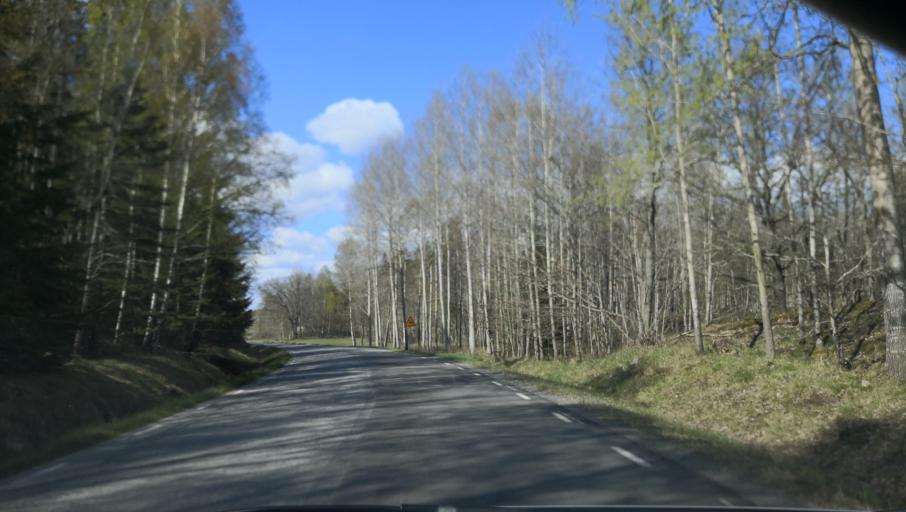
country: SE
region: Stockholm
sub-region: Varmdo Kommun
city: Hemmesta
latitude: 59.4003
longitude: 18.5106
